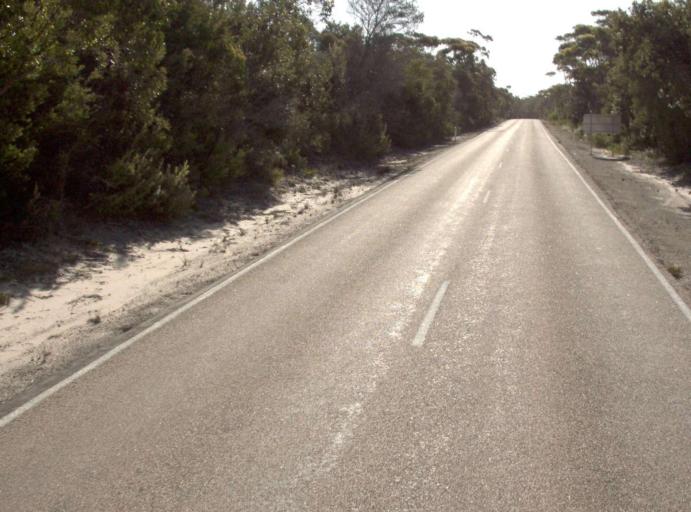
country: AU
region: Victoria
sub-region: East Gippsland
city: Lakes Entrance
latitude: -37.7976
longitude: 148.7008
